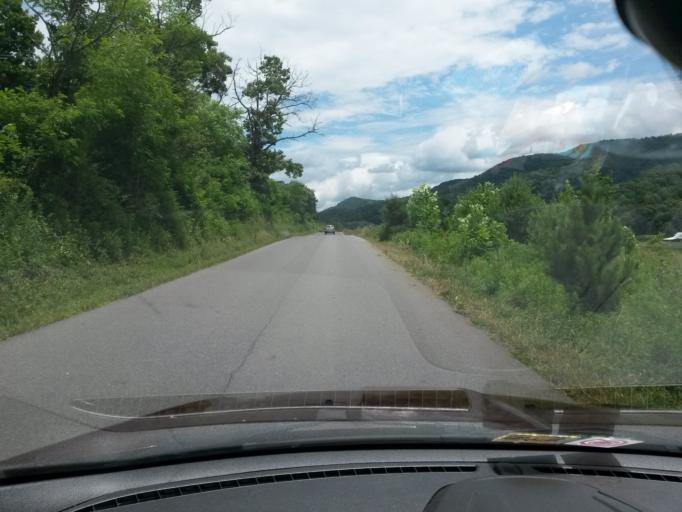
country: US
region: West Virginia
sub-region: Monroe County
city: Union
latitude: 37.5004
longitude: -80.5955
